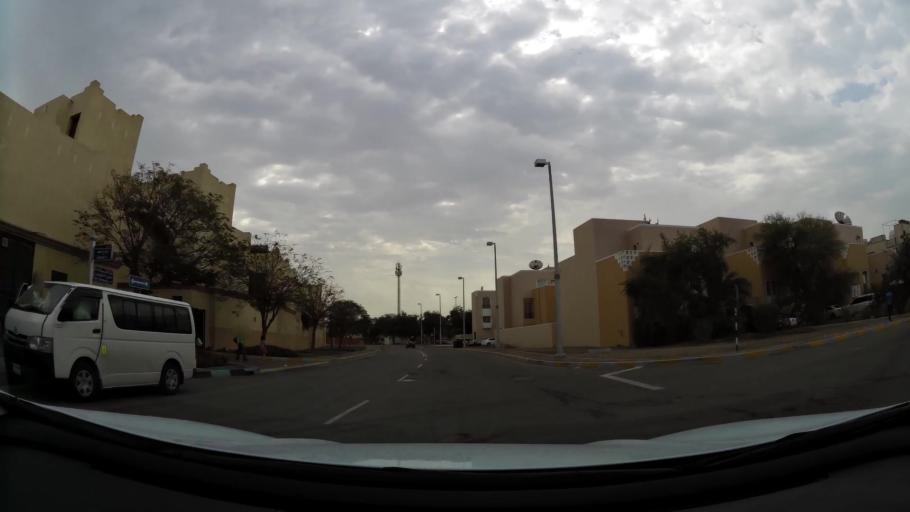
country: AE
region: Abu Dhabi
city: Abu Dhabi
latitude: 24.4469
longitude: 54.4083
